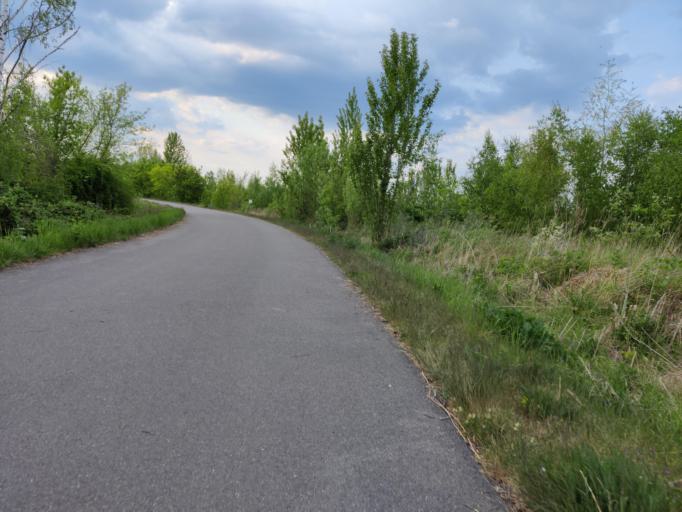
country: DE
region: Saxony
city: Rotha
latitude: 51.2277
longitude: 12.4437
